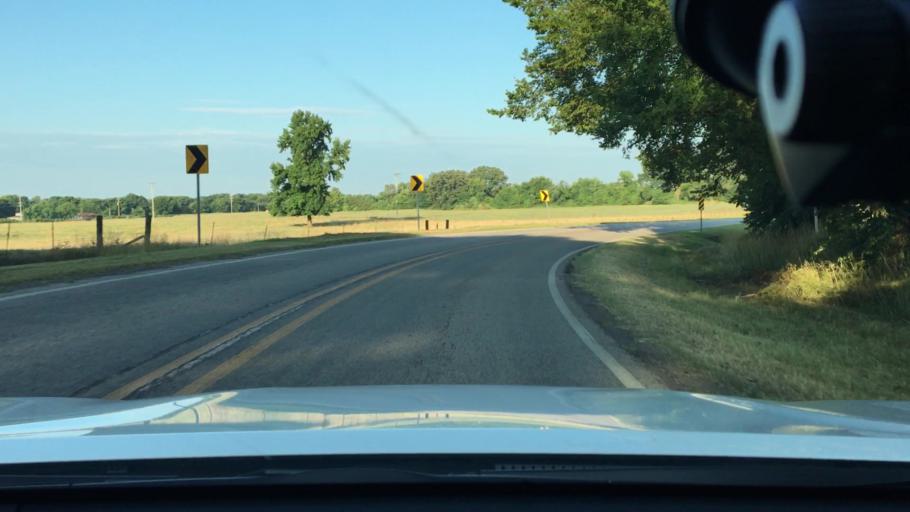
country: US
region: Arkansas
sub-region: Johnson County
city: Coal Hill
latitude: 35.3406
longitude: -93.5969
